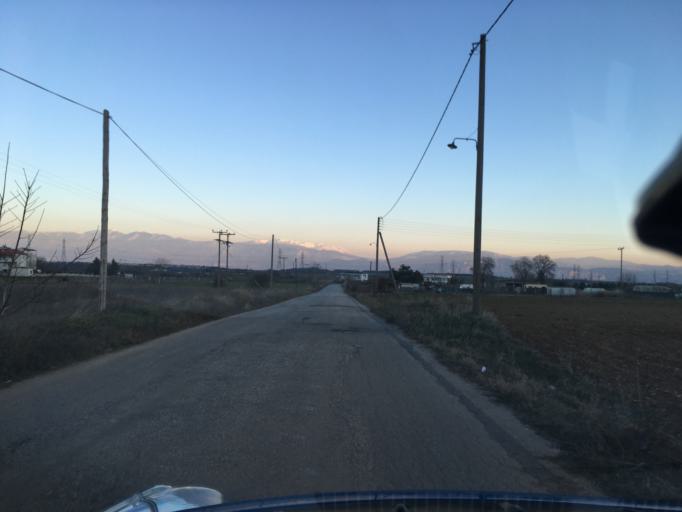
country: GR
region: West Macedonia
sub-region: Nomos Kozanis
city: Kozani
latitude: 40.2579
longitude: 21.7549
